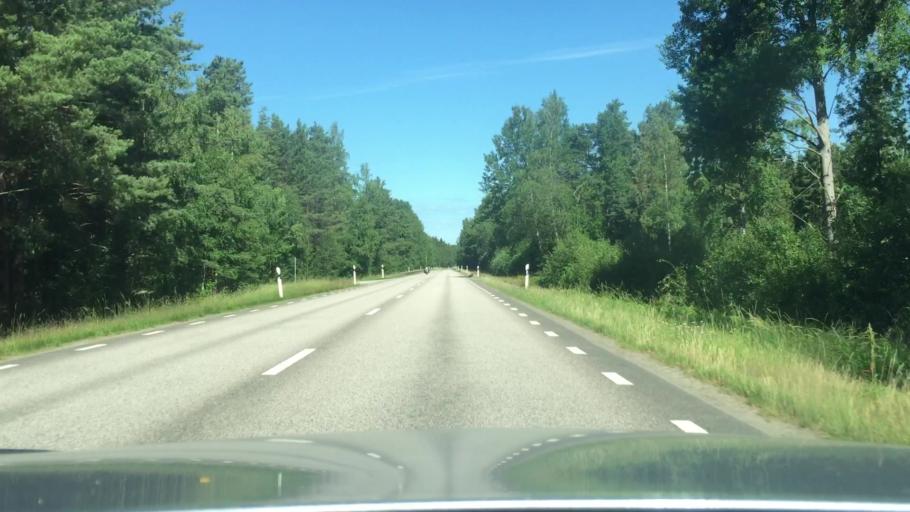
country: SE
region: Vaestra Goetaland
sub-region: Mariestads Kommun
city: Mariestad
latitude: 58.6726
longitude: 13.8544
